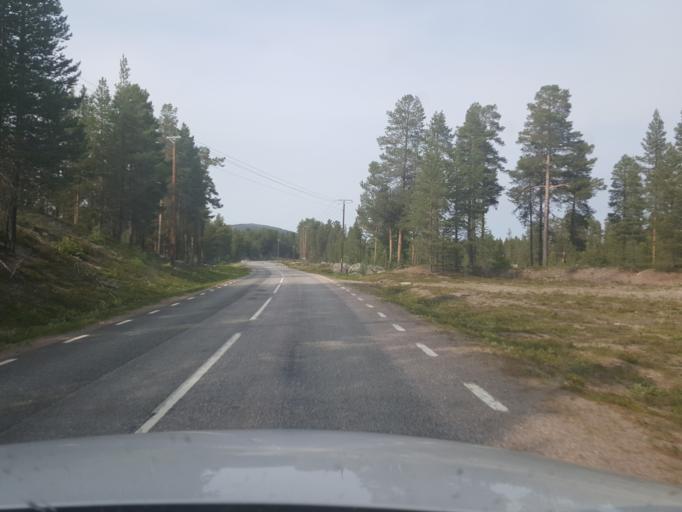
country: SE
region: Norrbotten
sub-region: Arjeplogs Kommun
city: Arjeplog
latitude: 65.8365
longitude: 18.0248
